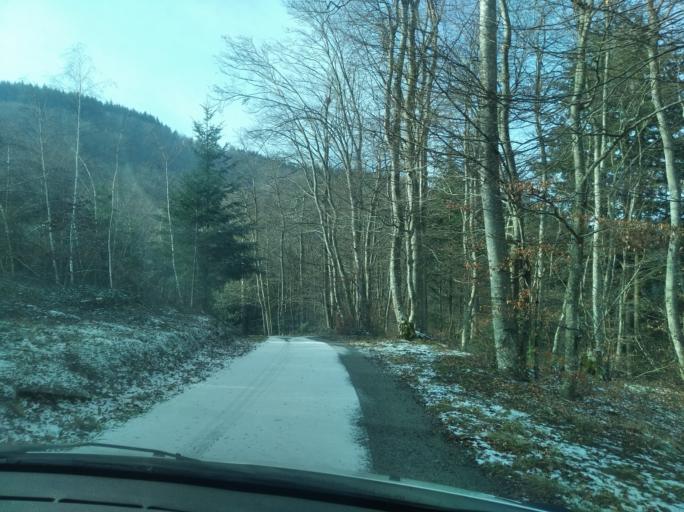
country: FR
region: Rhone-Alpes
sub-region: Departement de la Loire
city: La Pacaudiere
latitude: 46.1496
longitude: 3.7572
